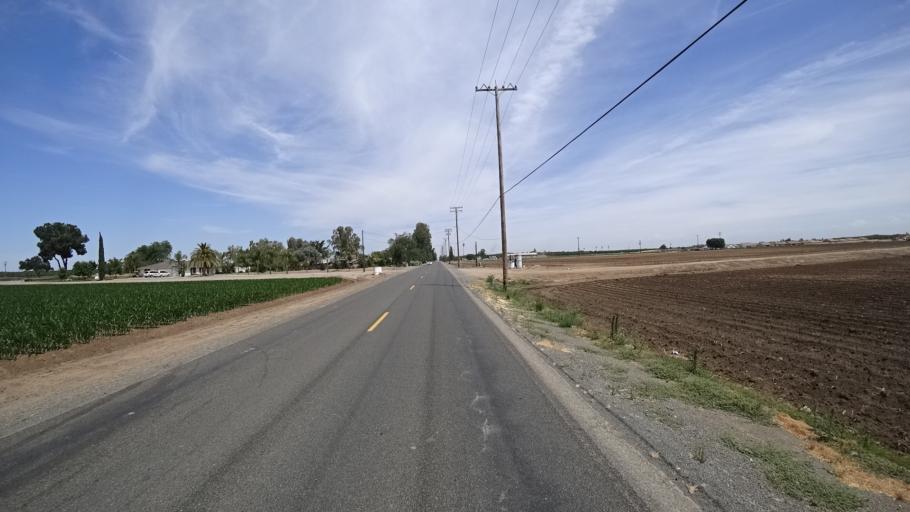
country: US
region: California
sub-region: Kings County
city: Armona
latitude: 36.3479
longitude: -119.6910
